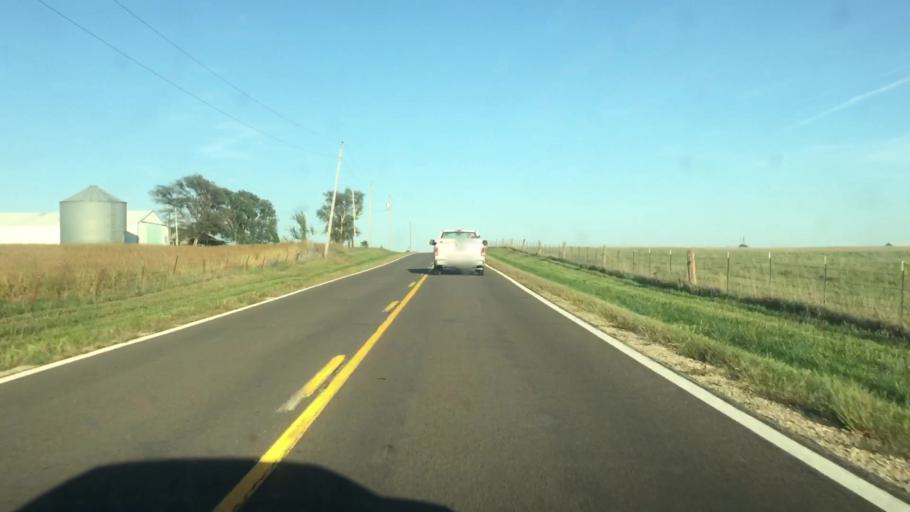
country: US
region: Kansas
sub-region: Brown County
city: Horton
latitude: 39.5515
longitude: -95.4453
